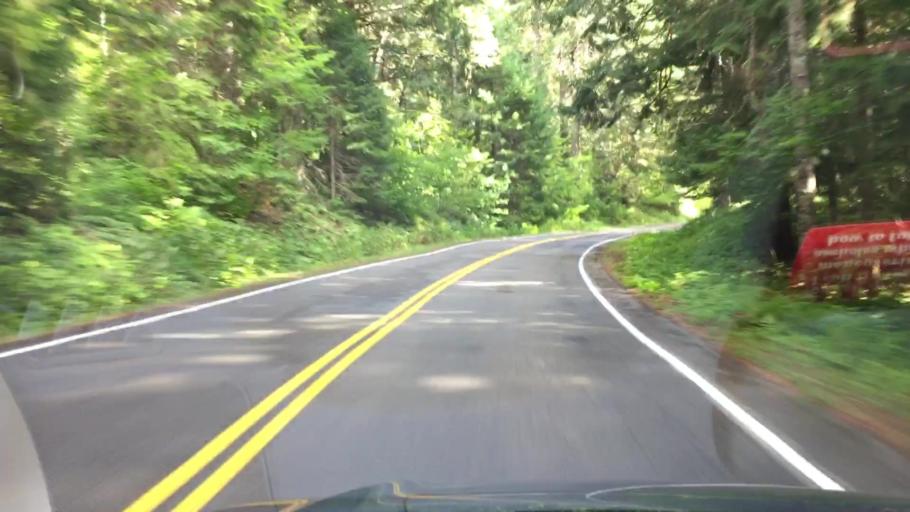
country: US
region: Washington
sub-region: Pierce County
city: Buckley
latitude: 46.7399
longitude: -121.6128
